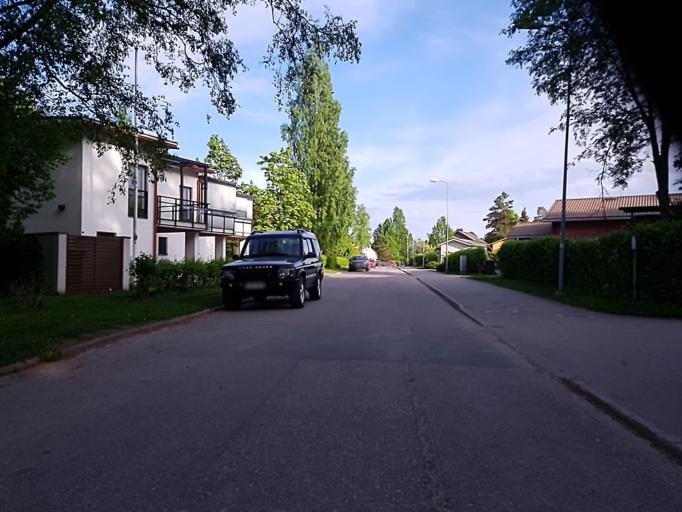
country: FI
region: Uusimaa
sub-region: Helsinki
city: Helsinki
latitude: 60.2510
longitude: 24.9250
